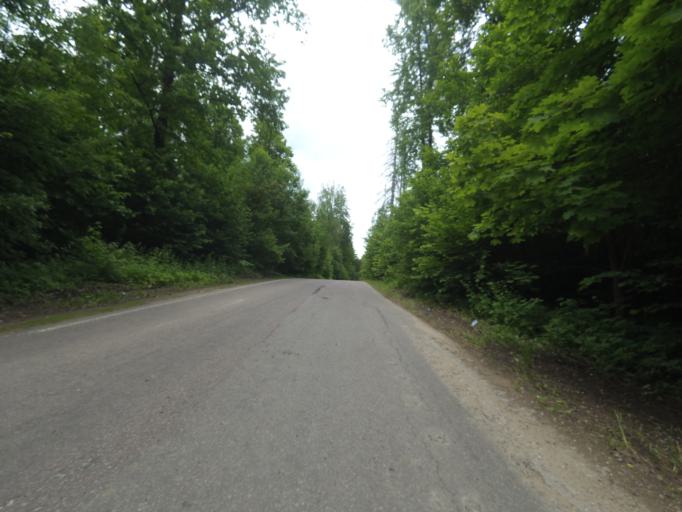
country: RU
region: Moskovskaya
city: Marfino
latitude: 56.0450
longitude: 37.6124
